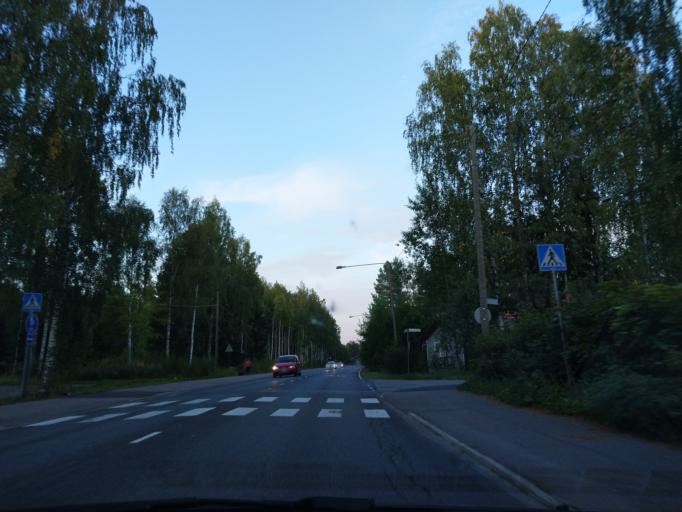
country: FI
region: Uusimaa
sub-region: Helsinki
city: Tuusula
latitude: 60.3577
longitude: 25.0565
